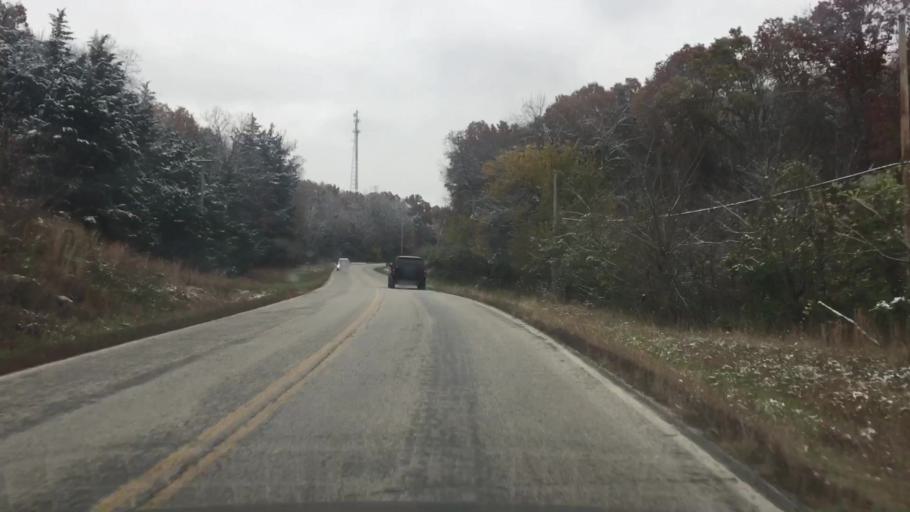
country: US
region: Missouri
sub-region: Saint Clair County
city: Osceola
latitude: 38.0434
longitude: -93.6919
